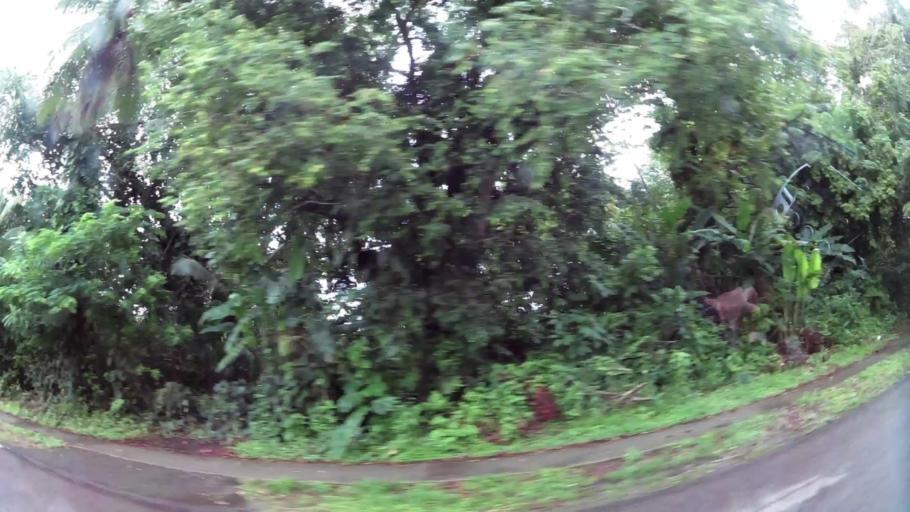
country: PA
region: Panama
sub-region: Distrito de Panama
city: Ancon
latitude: 9.0046
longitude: -79.5725
